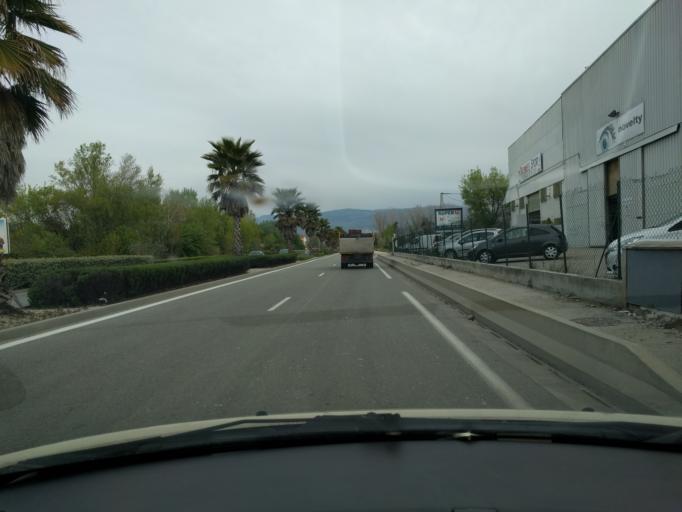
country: FR
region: Provence-Alpes-Cote d'Azur
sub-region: Departement des Alpes-Maritimes
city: Mandelieu-la-Napoule
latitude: 43.5629
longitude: 6.9502
